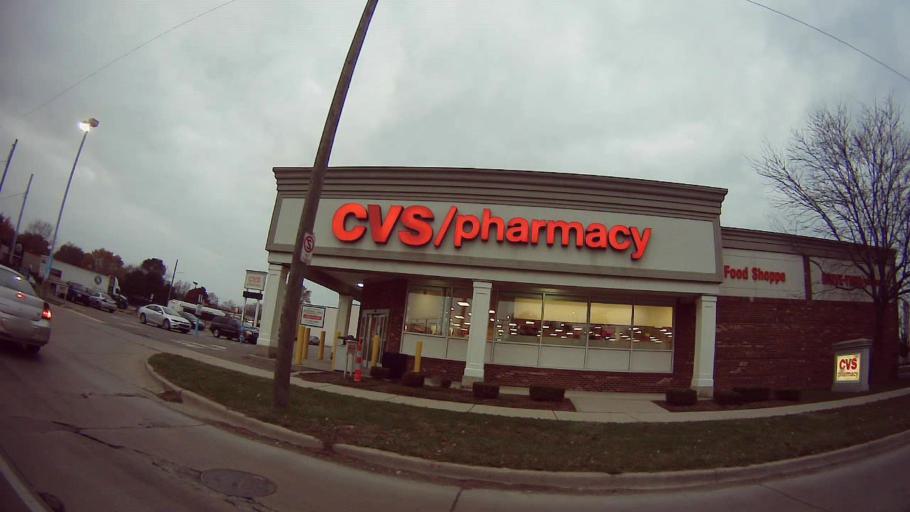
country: US
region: Michigan
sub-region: Macomb County
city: Warren
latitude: 42.4413
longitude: -83.0238
